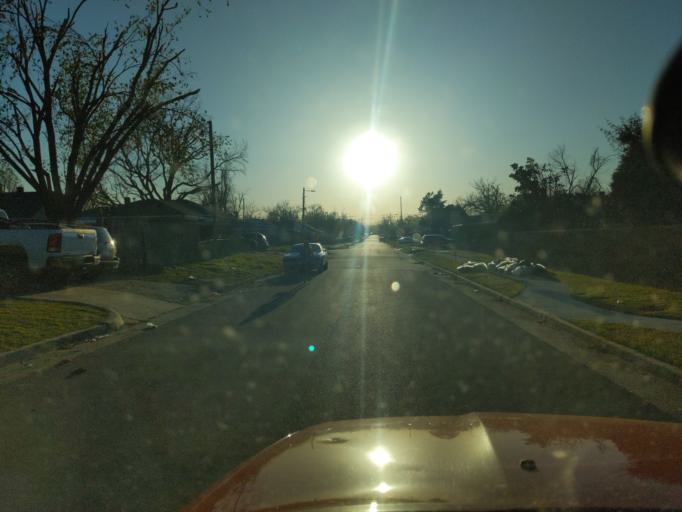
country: US
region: Oklahoma
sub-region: Oklahoma County
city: Oklahoma City
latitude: 35.4153
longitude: -97.5217
